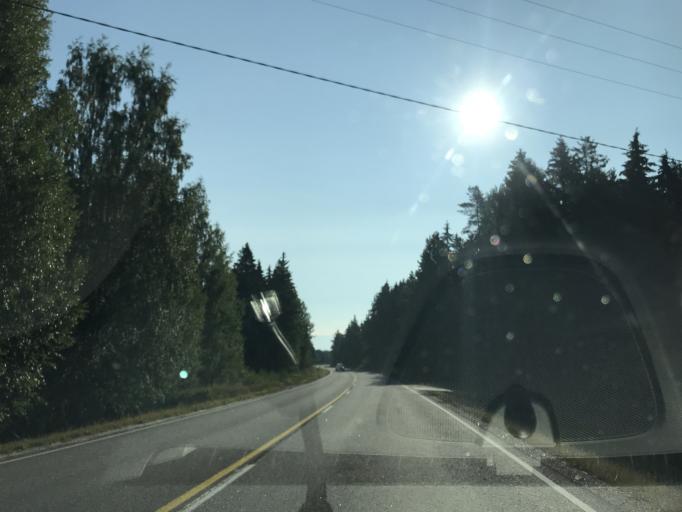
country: FI
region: Uusimaa
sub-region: Porvoo
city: Pukkila
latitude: 60.7684
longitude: 25.5119
